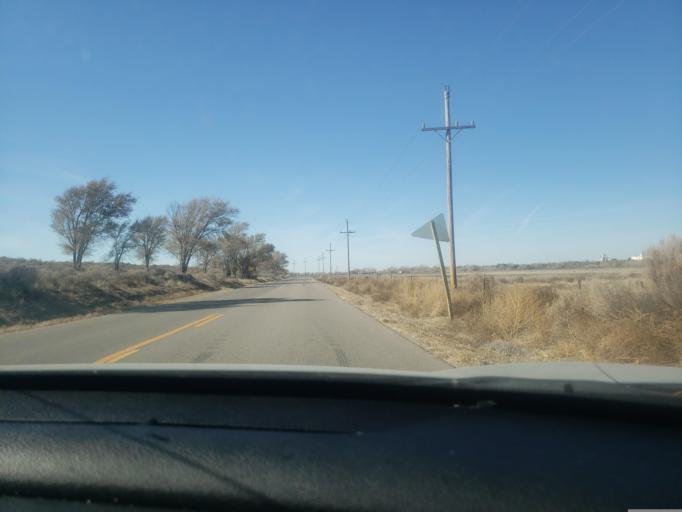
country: US
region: Kansas
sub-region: Finney County
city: Garden City
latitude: 37.9511
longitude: -100.8567
